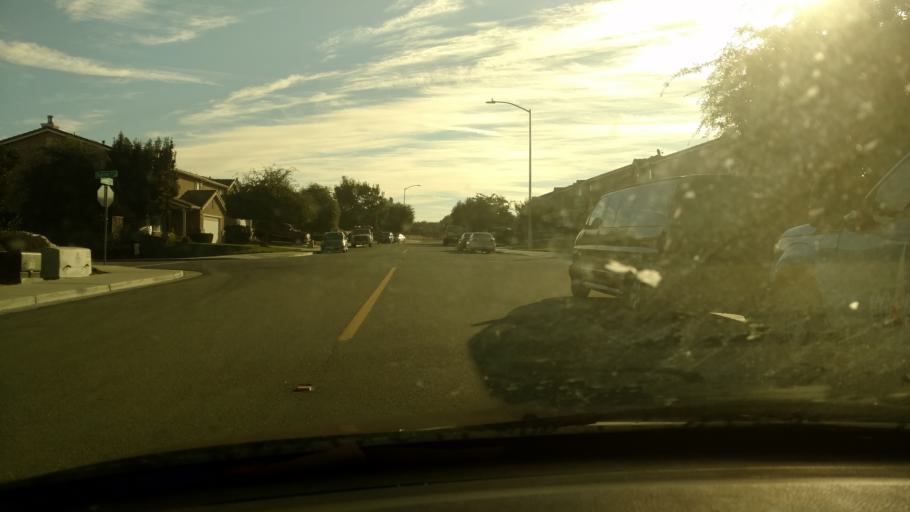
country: US
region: California
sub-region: San Benito County
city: Ridgemark
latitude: 36.8210
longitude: -121.3721
